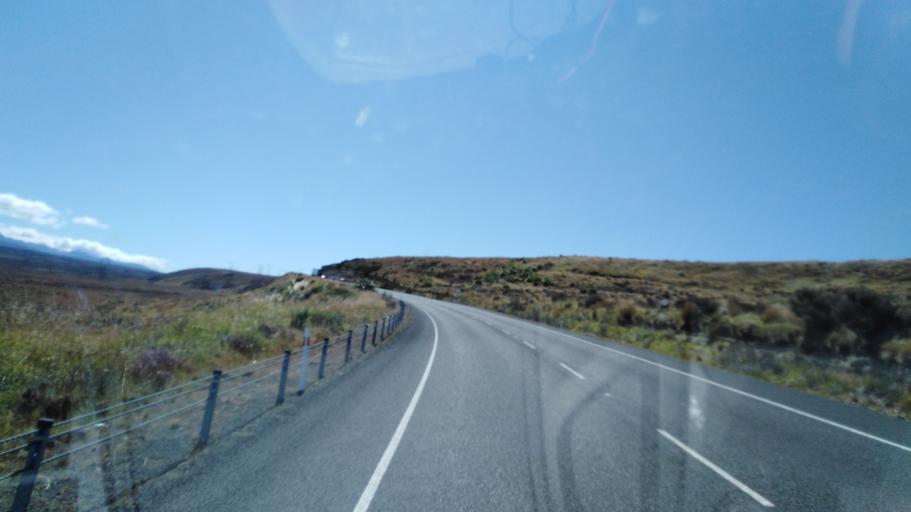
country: NZ
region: Manawatu-Wanganui
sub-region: Ruapehu District
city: Waiouru
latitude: -39.3876
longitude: 175.7083
